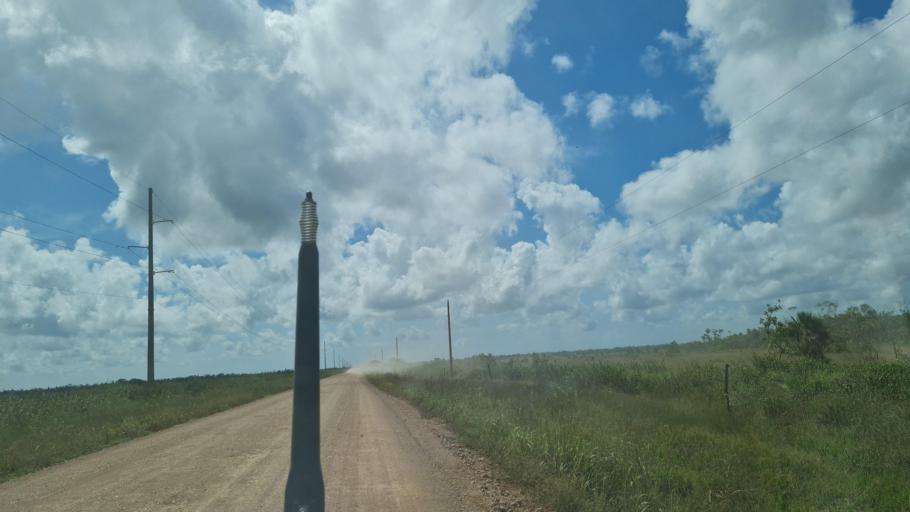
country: NI
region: Atlantico Norte (RAAN)
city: Puerto Cabezas
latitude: 14.1096
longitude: -83.5949
